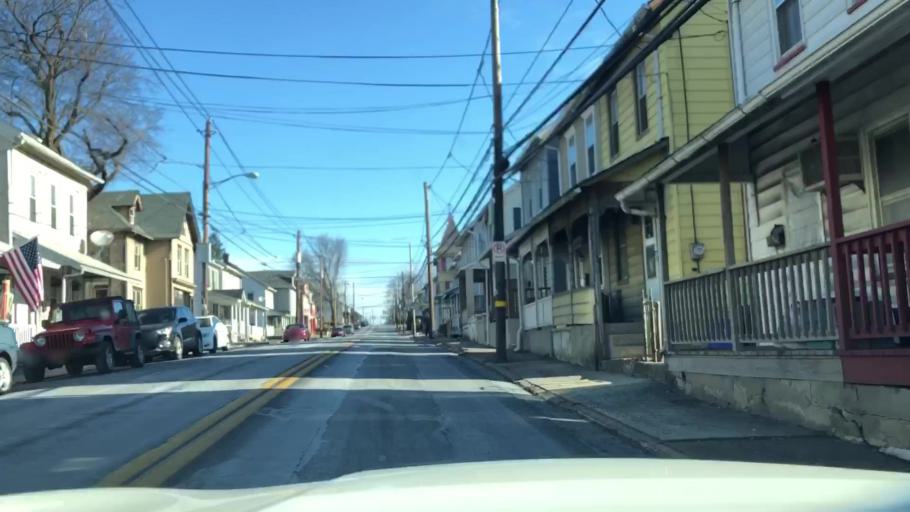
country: US
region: Pennsylvania
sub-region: Lehigh County
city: Catasauqua
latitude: 40.6518
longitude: -75.4616
